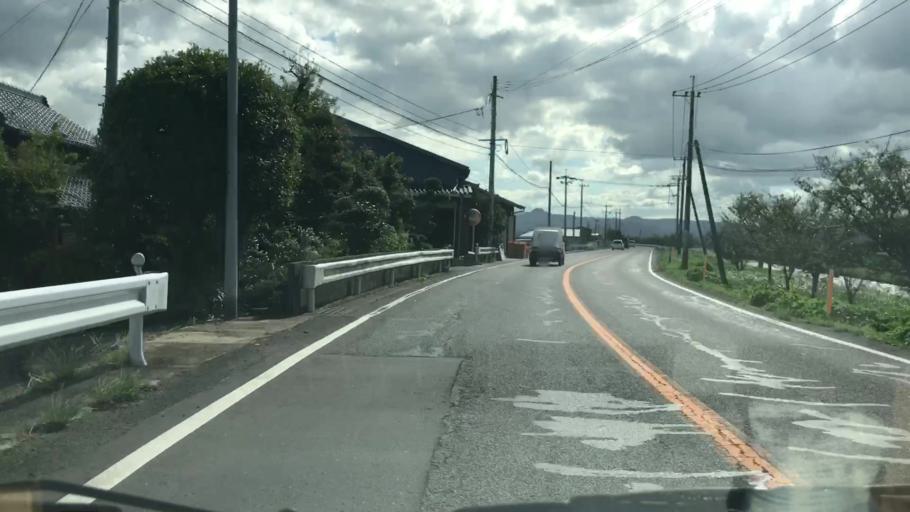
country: JP
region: Saga Prefecture
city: Kashima
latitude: 33.1581
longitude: 130.1623
